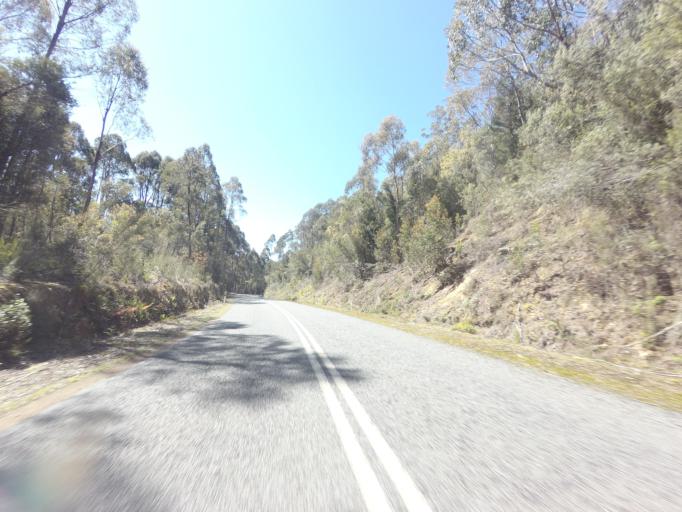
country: AU
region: Tasmania
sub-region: Huon Valley
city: Geeveston
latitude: -42.7842
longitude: 146.3993
